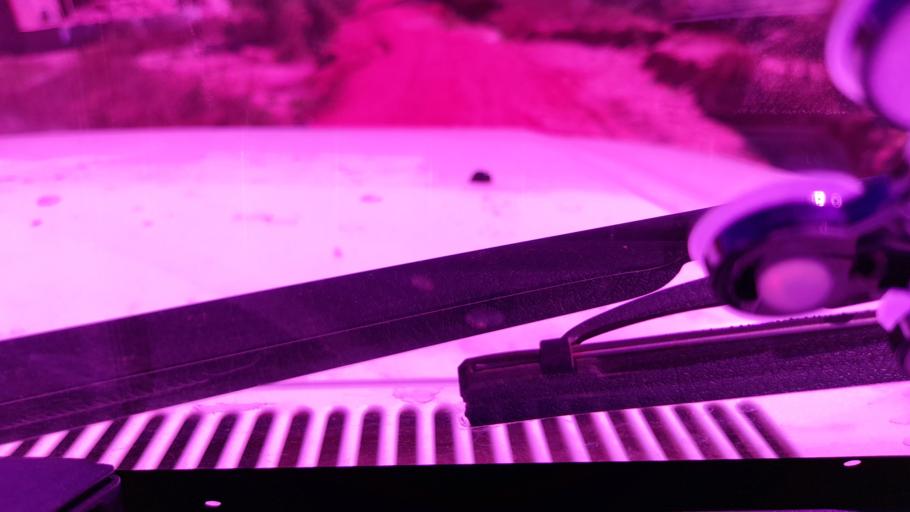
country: SN
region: Ziguinchor
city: Adeane
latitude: 12.4085
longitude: -15.7913
